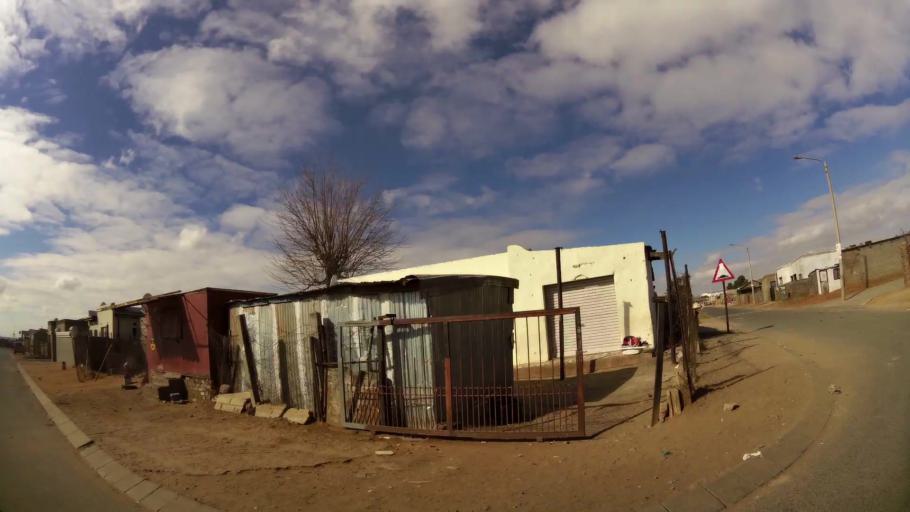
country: ZA
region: Gauteng
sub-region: City of Johannesburg Metropolitan Municipality
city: Modderfontein
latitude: -26.0451
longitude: 28.1763
